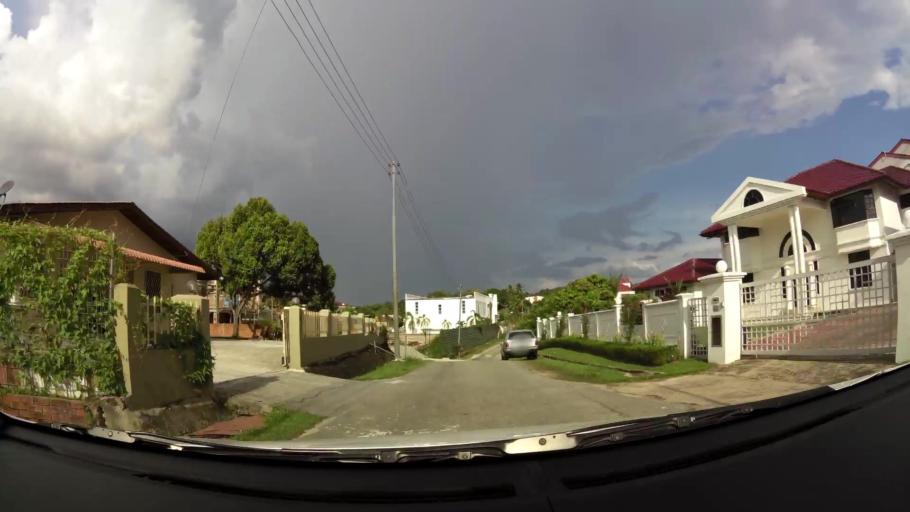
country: BN
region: Brunei and Muara
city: Bandar Seri Begawan
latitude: 4.9642
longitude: 114.9737
